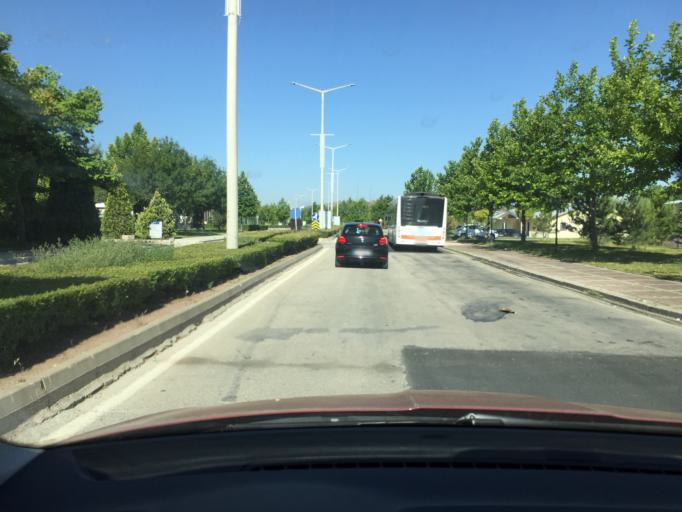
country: TR
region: Eskisehir
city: Eskisehir
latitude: 39.7531
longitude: 30.4851
